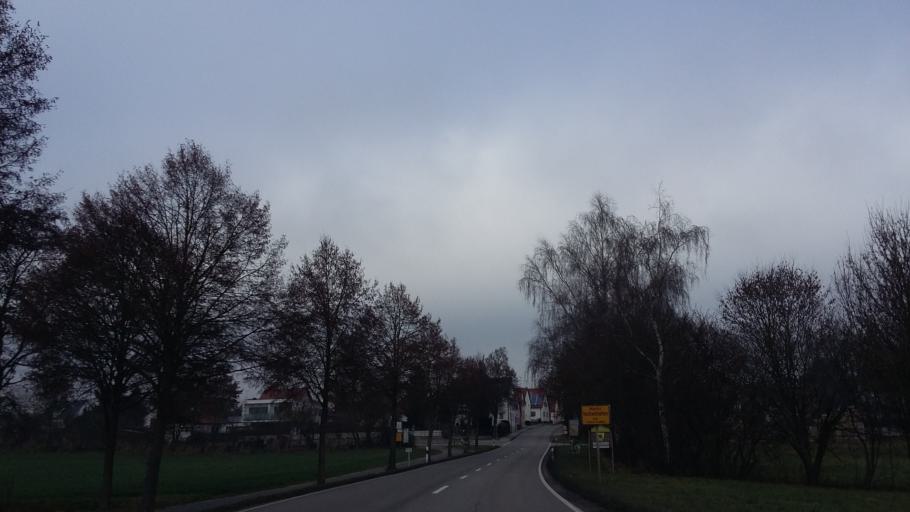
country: DE
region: Bavaria
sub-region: Swabia
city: Inchenhofen
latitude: 48.5062
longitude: 11.1165
